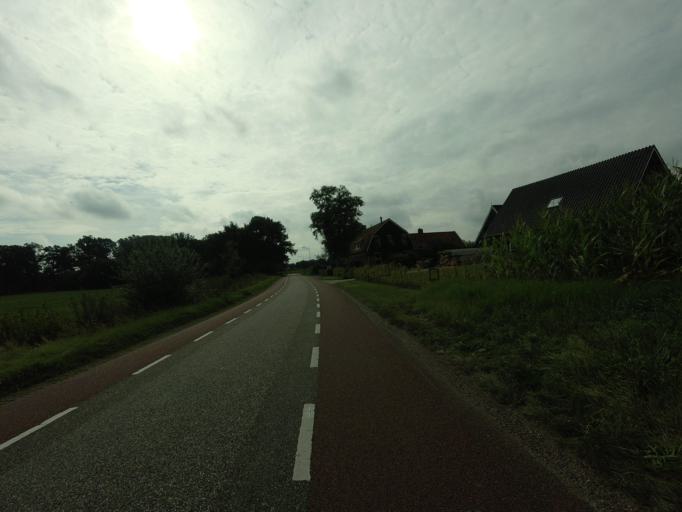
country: DE
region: Lower Saxony
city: Nordhorn
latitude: 52.3913
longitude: 7.0013
